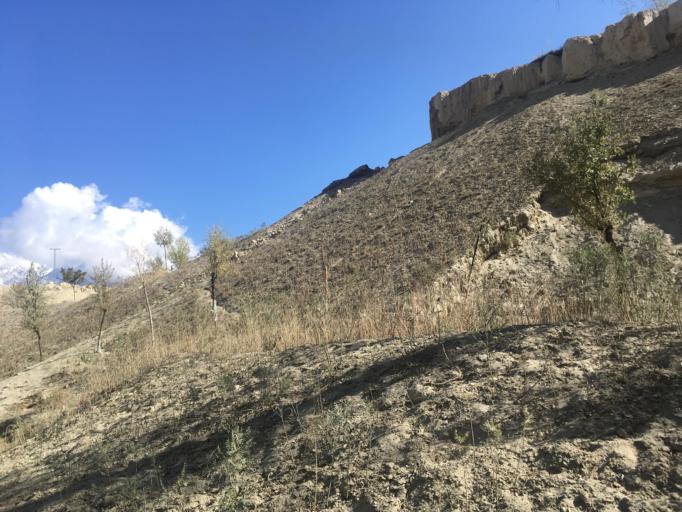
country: PK
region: Gilgit-Baltistan
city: Skardu
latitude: 35.3331
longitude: 75.5208
